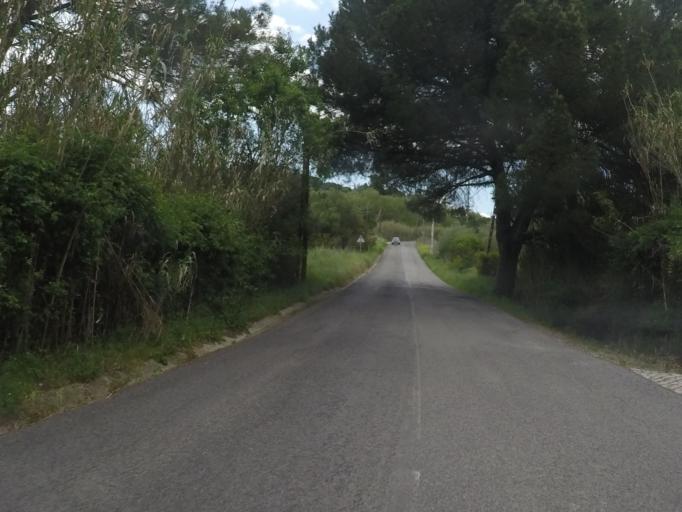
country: PT
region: Setubal
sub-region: Palmela
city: Quinta do Anjo
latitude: 38.5061
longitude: -8.9998
